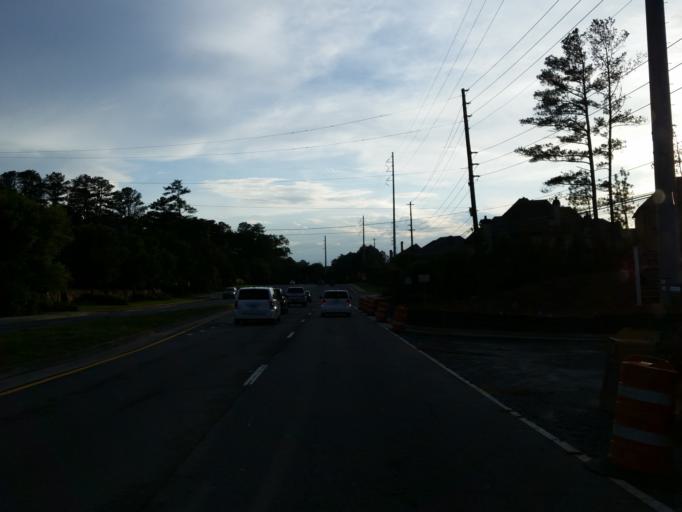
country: US
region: Georgia
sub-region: Fulton County
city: Roswell
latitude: 34.0017
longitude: -84.3998
